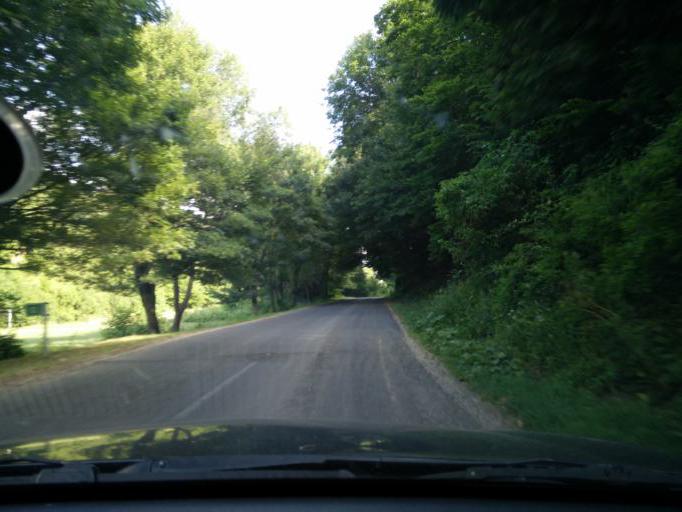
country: HU
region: Komarom-Esztergom
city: Tardos
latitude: 47.6701
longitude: 18.4431
